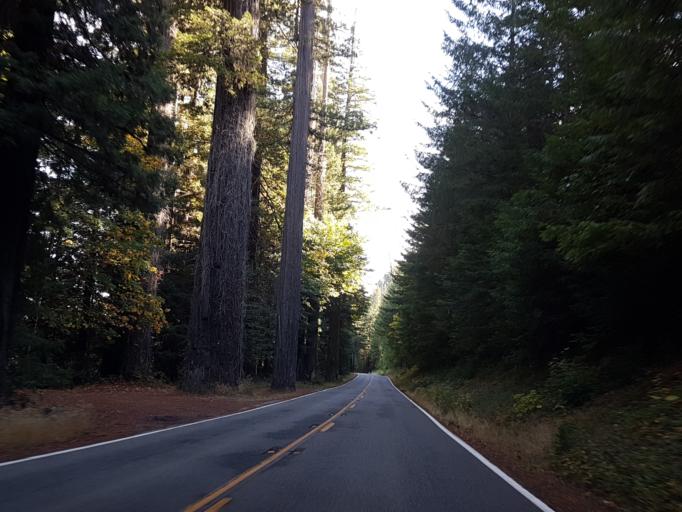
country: US
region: California
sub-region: Humboldt County
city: Rio Dell
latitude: 40.4308
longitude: -123.9845
